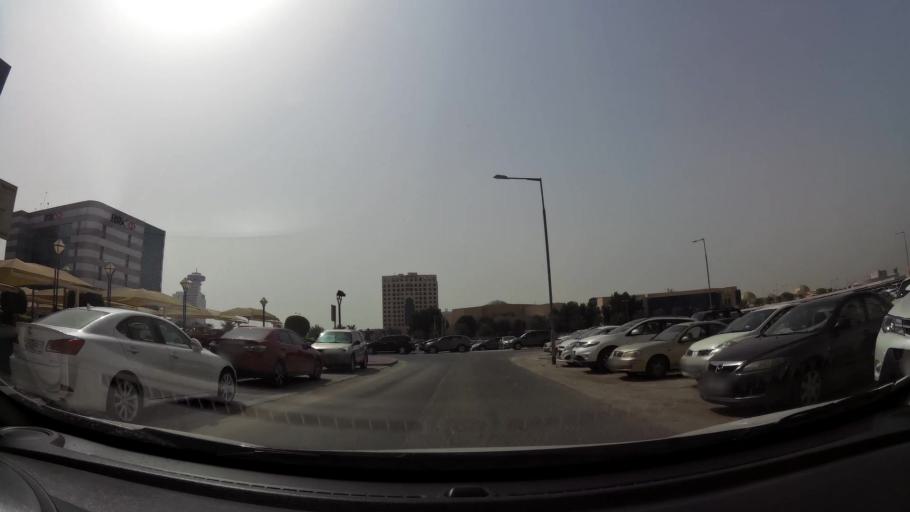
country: BH
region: Manama
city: Jidd Hafs
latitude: 26.2358
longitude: 50.5404
